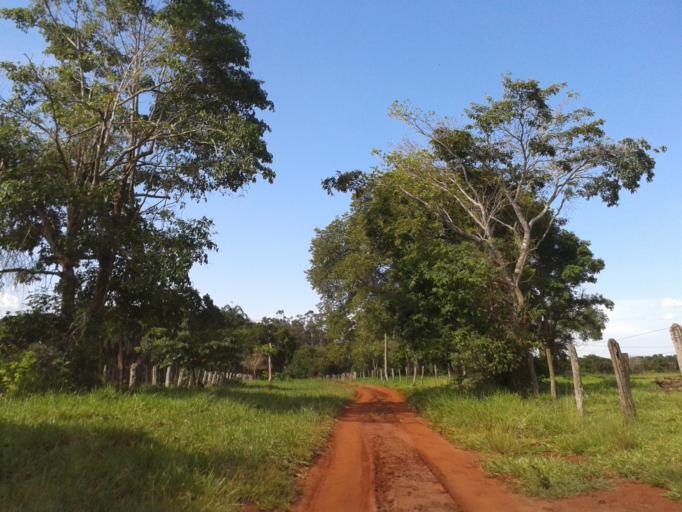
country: BR
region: Minas Gerais
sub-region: Santa Vitoria
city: Santa Vitoria
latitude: -19.1140
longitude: -50.5379
